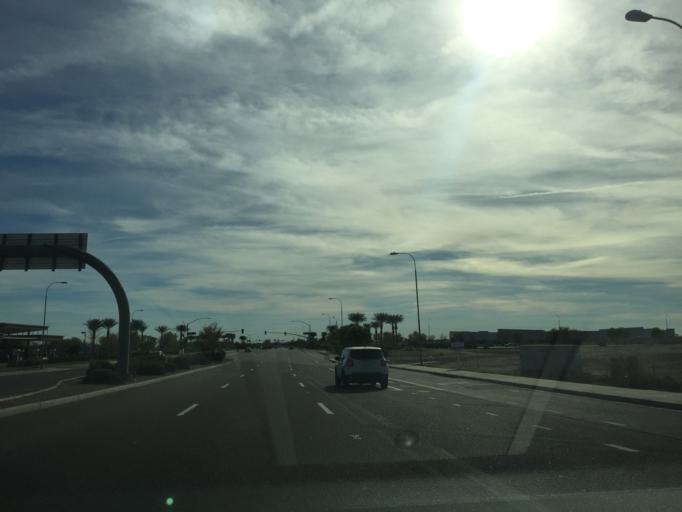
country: US
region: Arizona
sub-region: Maricopa County
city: Chandler
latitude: 33.2815
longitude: -111.8071
